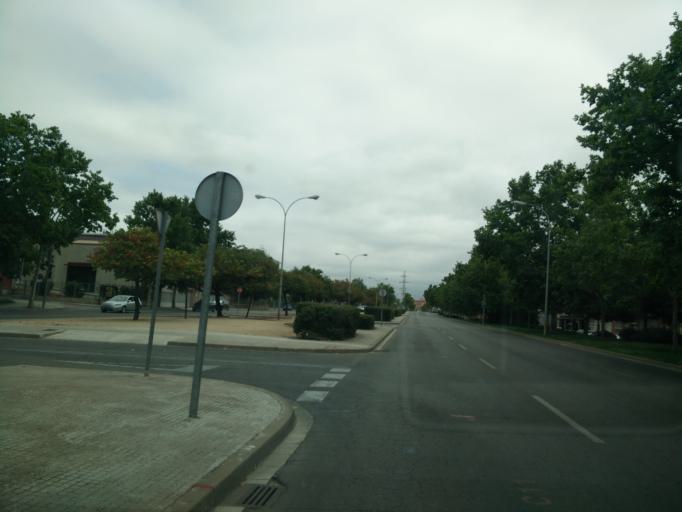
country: ES
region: Catalonia
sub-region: Provincia de Barcelona
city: Terrassa
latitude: 41.5801
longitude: 2.0201
